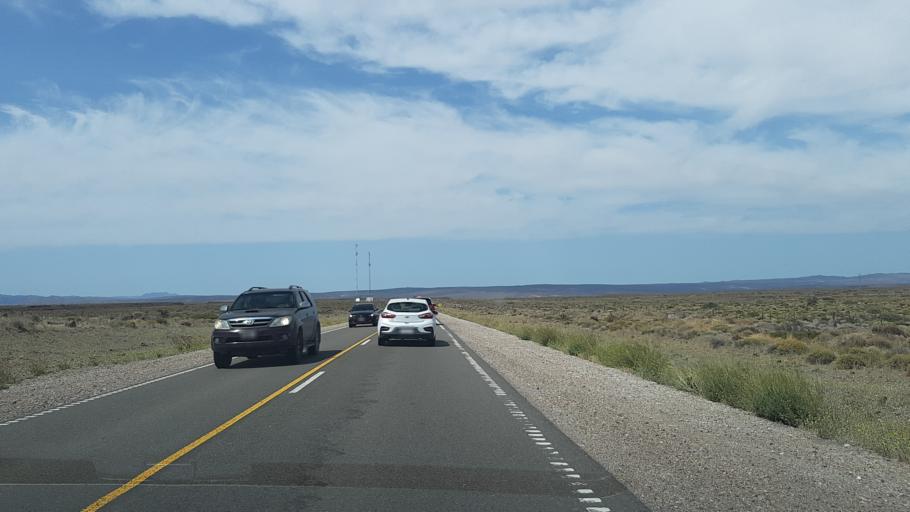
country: AR
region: Neuquen
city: Piedra del Aguila
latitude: -39.9901
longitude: -70.0401
